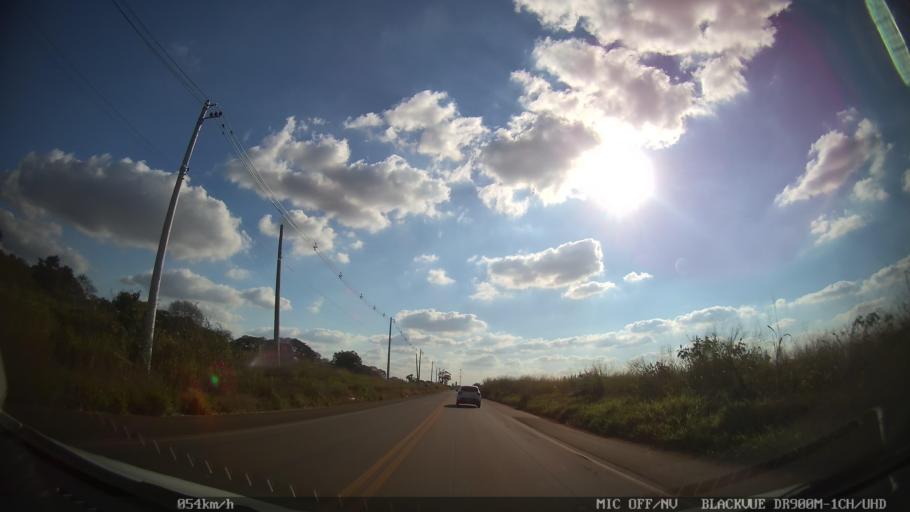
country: BR
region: Sao Paulo
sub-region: Americana
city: Americana
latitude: -22.7824
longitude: -47.3635
